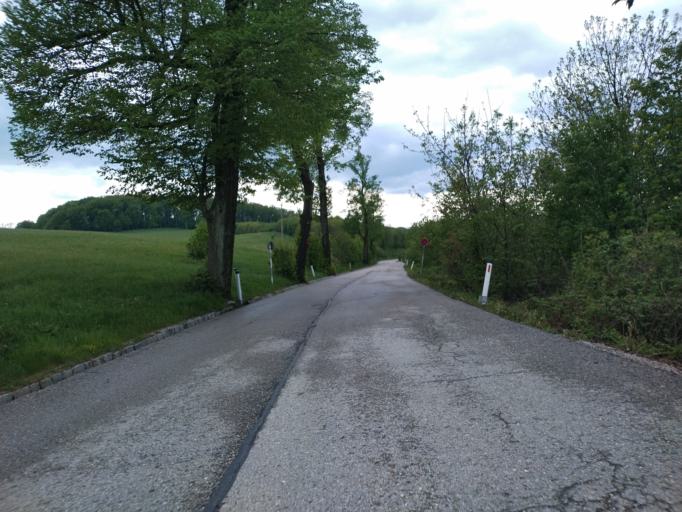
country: AT
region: Lower Austria
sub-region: Politischer Bezirk Wien-Umgebung
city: Mauerbach
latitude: 48.2467
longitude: 16.2283
